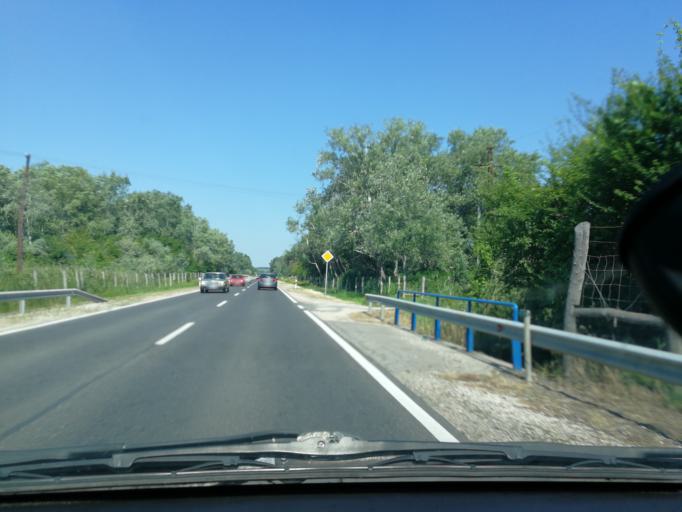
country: HU
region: Fejer
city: Pakozd
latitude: 47.1834
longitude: 18.5303
